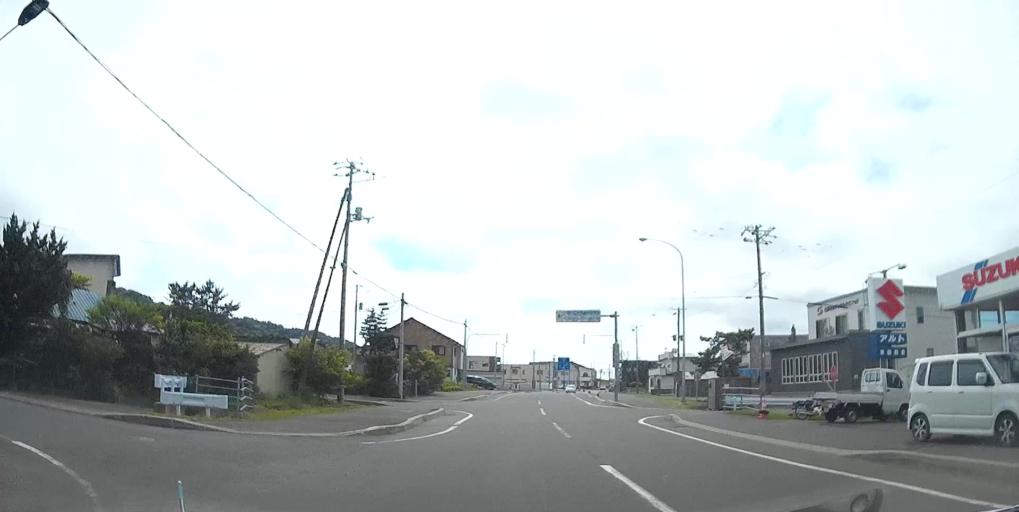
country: JP
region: Hokkaido
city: Kamiiso
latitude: 41.9703
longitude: 140.1397
